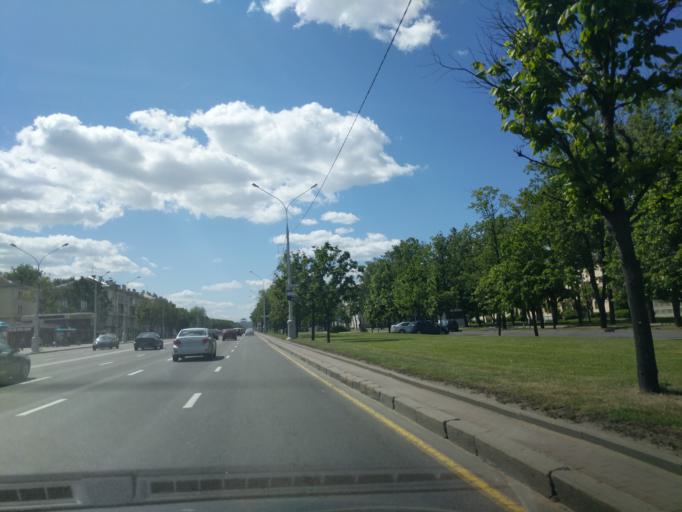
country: BY
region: Minsk
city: Minsk
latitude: 53.9289
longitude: 27.6304
